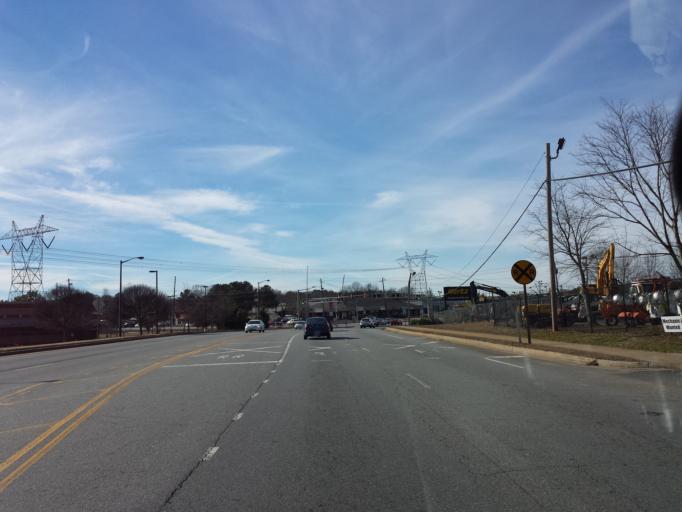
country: US
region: Georgia
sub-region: Cobb County
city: Marietta
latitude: 33.9948
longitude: -84.5240
